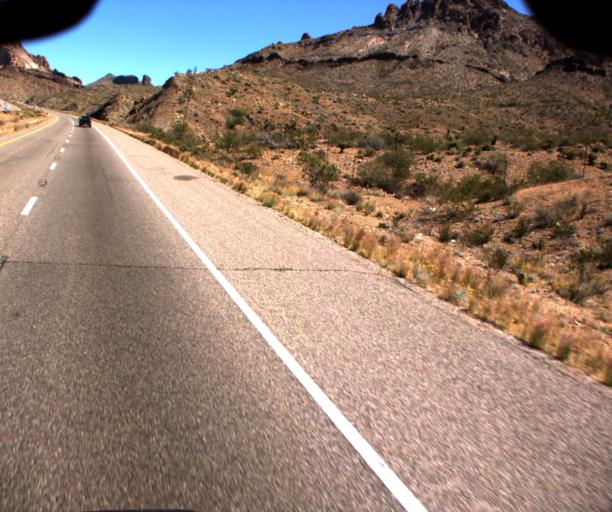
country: US
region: Nevada
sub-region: Clark County
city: Laughlin
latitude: 35.1988
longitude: -114.4041
